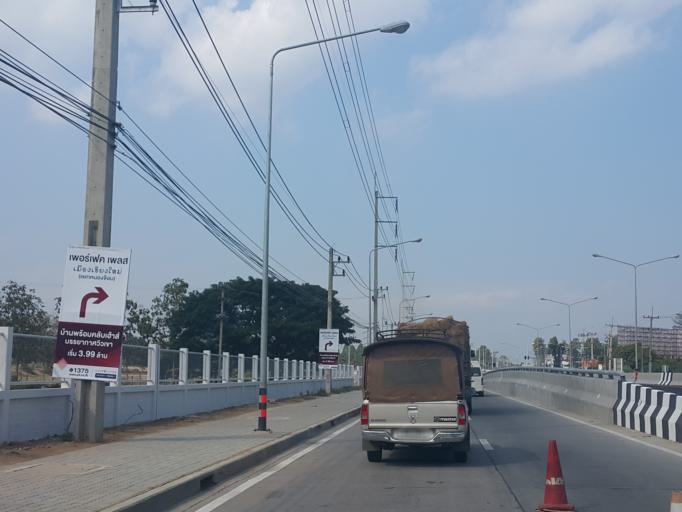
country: TH
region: Chiang Mai
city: Chiang Mai
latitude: 18.8637
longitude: 98.9651
